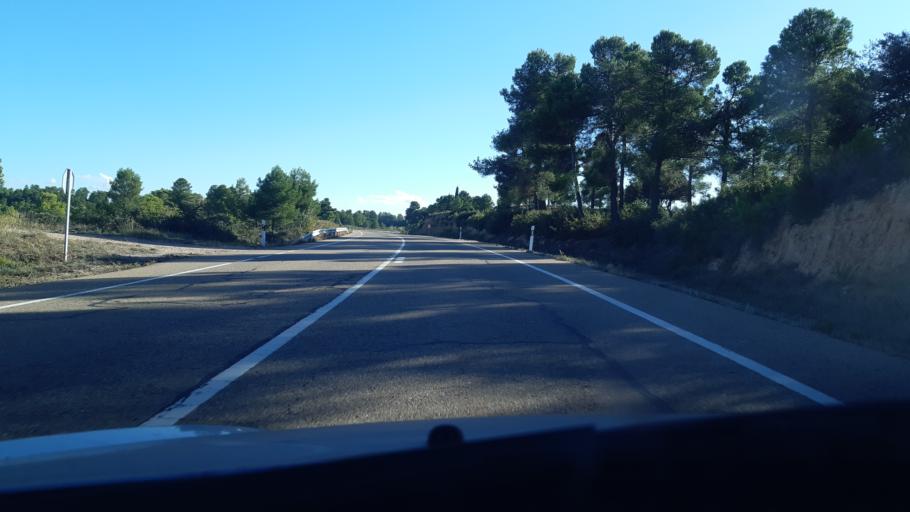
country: ES
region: Aragon
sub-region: Provincia de Teruel
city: Valjunquera
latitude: 40.9416
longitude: -0.0120
